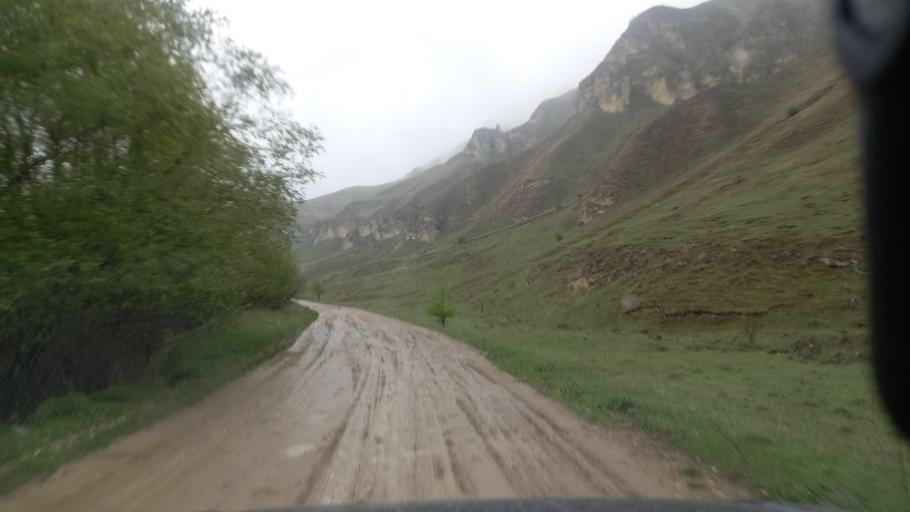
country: RU
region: Kabardino-Balkariya
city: Gundelen
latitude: 43.5984
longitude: 43.0454
